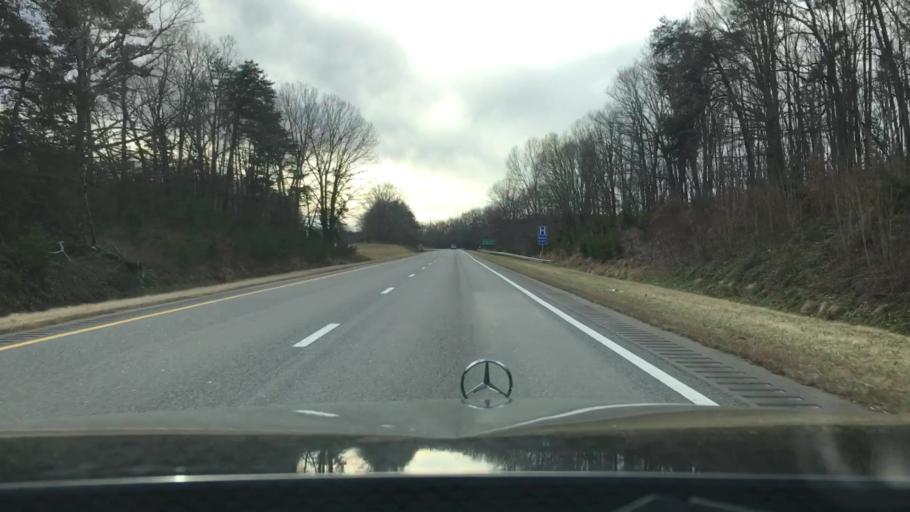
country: US
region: Virginia
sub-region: Pittsylvania County
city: Gretna
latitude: 36.9625
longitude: -79.3725
